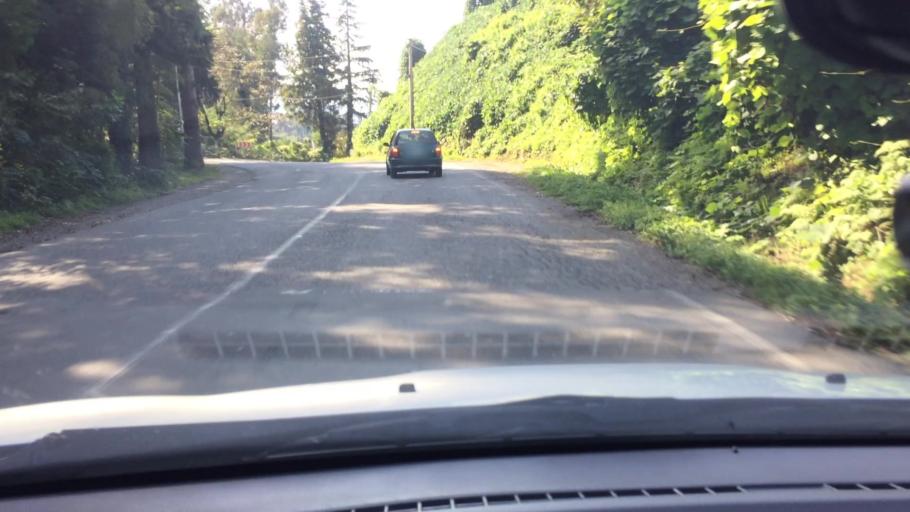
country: GE
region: Ajaria
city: Kobuleti
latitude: 41.7512
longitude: 41.7445
